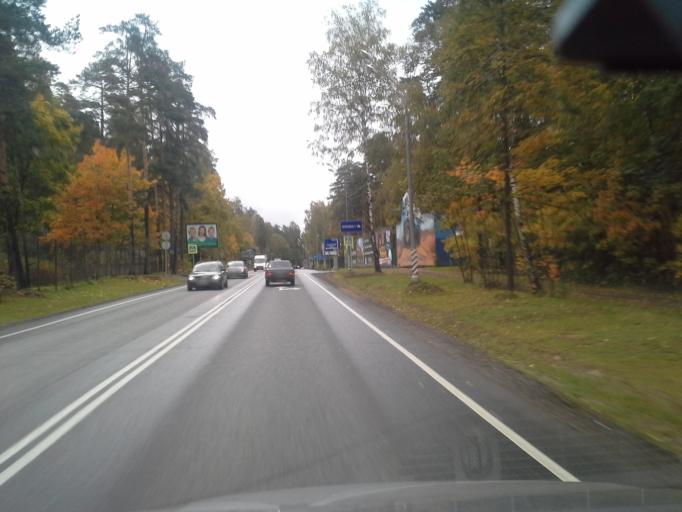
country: RU
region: Moskovskaya
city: Barvikha
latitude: 55.7356
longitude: 37.2283
